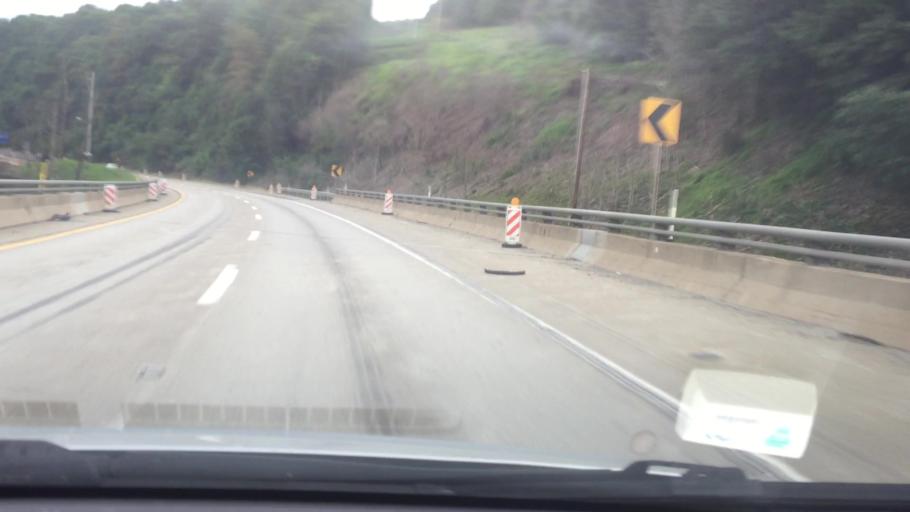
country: US
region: Pennsylvania
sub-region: Armstrong County
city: Freeport
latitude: 40.6539
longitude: -79.7251
